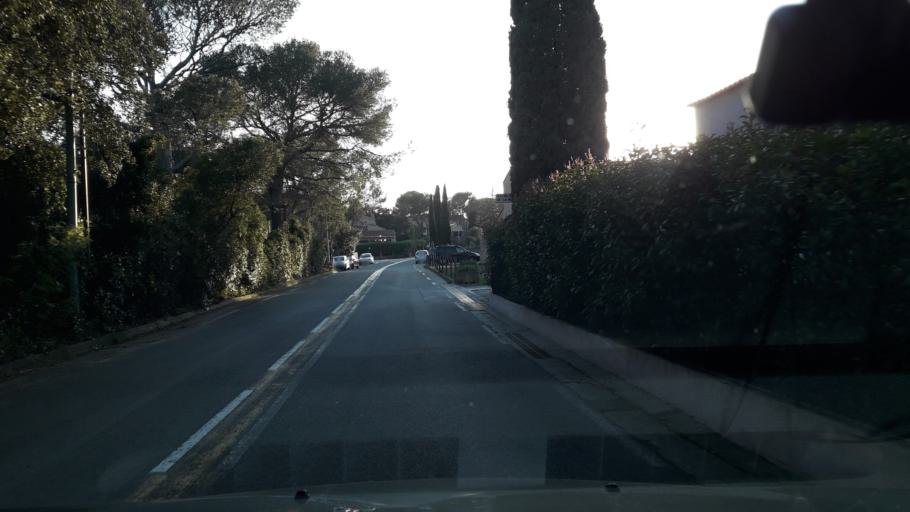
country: FR
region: Provence-Alpes-Cote d'Azur
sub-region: Departement du Var
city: Saint-Raphael
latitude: 43.4624
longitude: 6.7692
